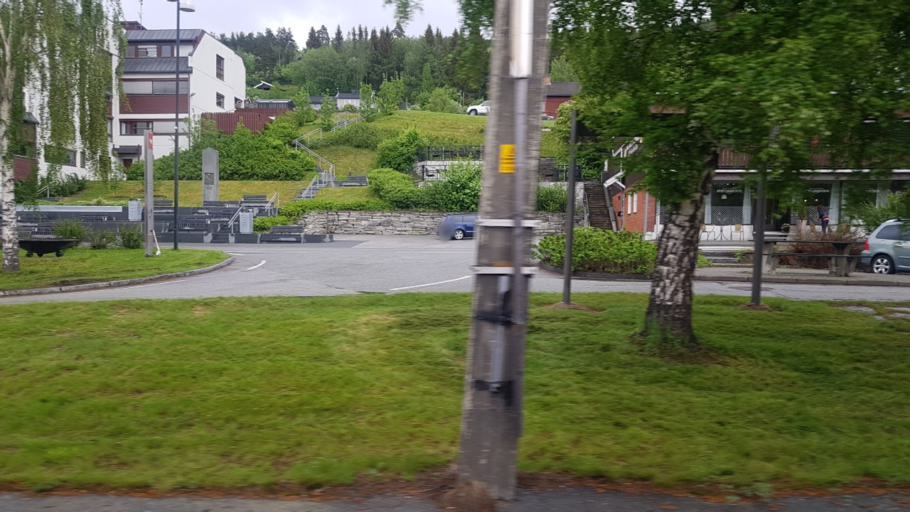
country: NO
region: Oppland
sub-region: Nord-Fron
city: Vinstra
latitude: 61.5975
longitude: 9.7341
